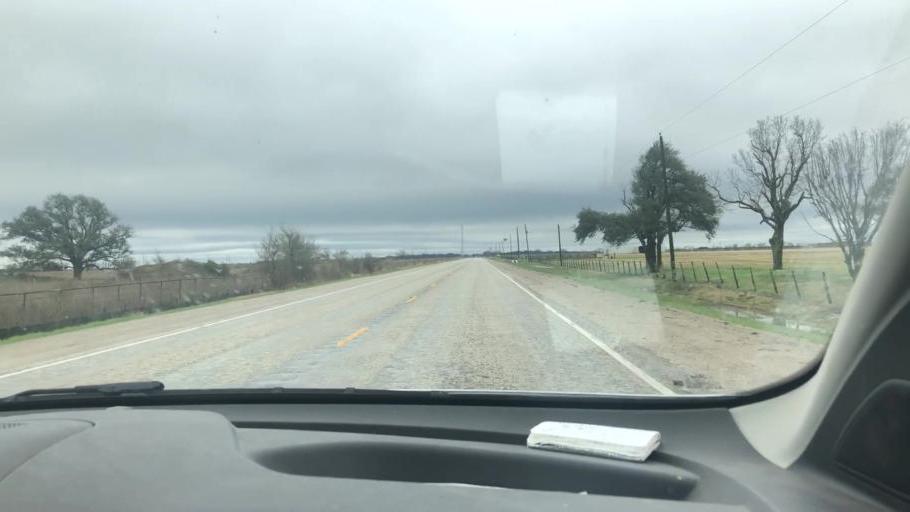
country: US
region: Texas
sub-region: Wharton County
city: Wharton
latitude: 29.2449
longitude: -96.0447
